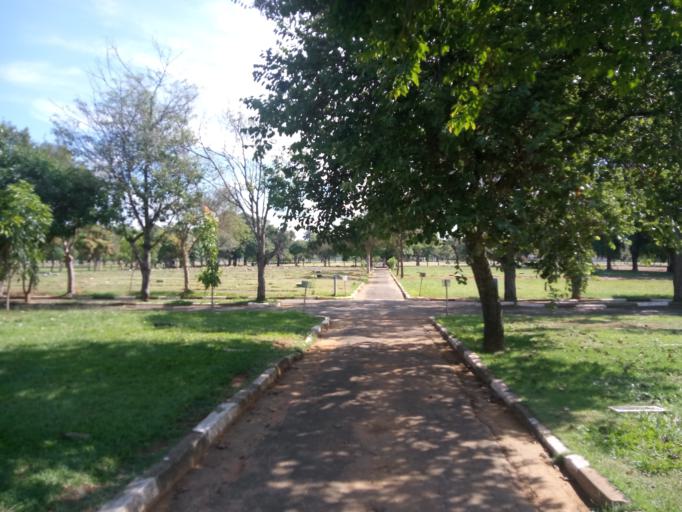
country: BR
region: Sao Paulo
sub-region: Campinas
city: Campinas
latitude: -22.8595
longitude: -47.1021
